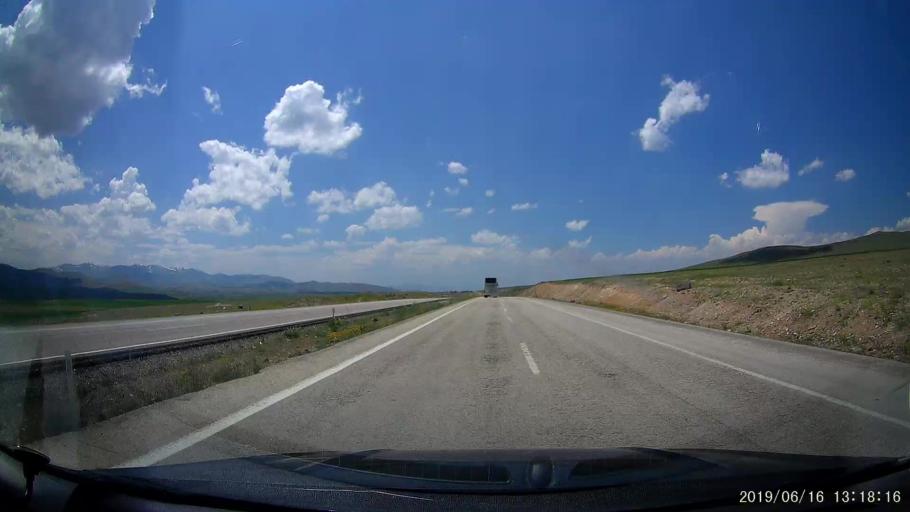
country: TR
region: Agri
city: Taslicay
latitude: 39.6300
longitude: 43.4342
